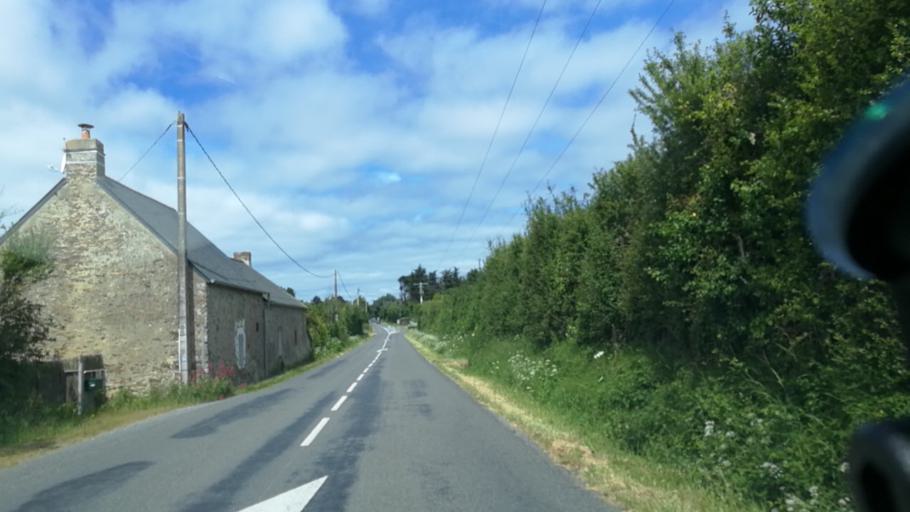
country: FR
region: Pays de la Loire
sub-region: Departement de la Loire-Atlantique
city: Mesquer
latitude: 47.4432
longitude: -2.4414
